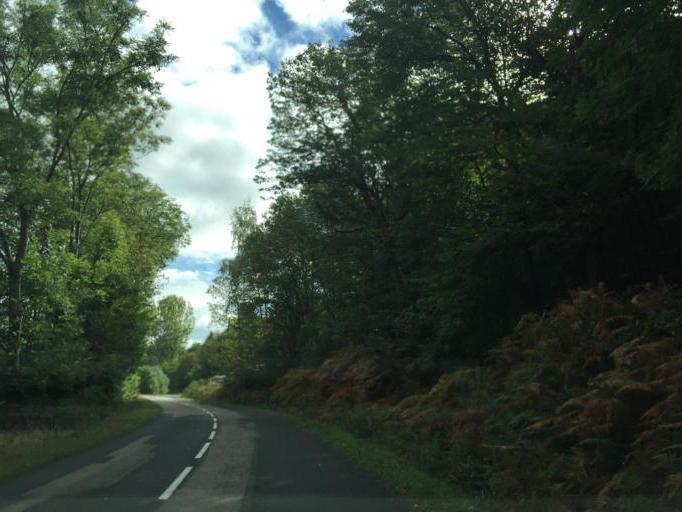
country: FR
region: Rhone-Alpes
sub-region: Departement de la Loire
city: Pelussin
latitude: 45.4630
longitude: 4.6697
